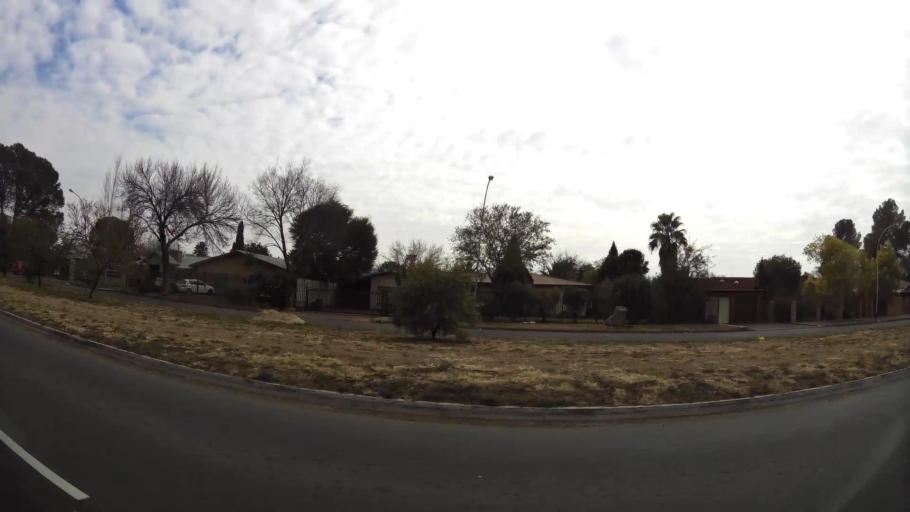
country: ZA
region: Orange Free State
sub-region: Mangaung Metropolitan Municipality
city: Bloemfontein
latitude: -29.1260
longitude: 26.1858
